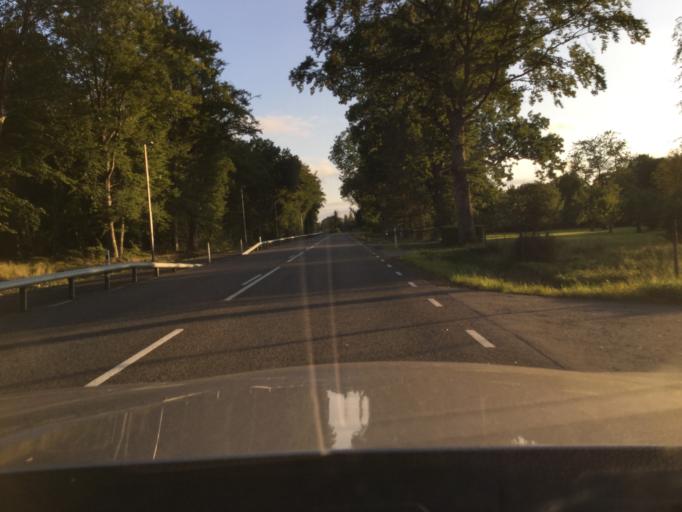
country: SE
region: Kronoberg
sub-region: Almhults Kommun
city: AElmhult
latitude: 56.6625
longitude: 14.2555
